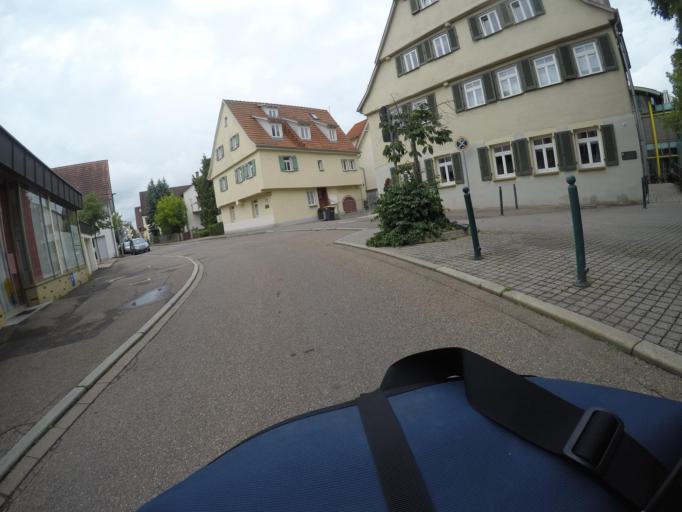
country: DE
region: Baden-Wuerttemberg
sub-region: Regierungsbezirk Stuttgart
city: Ditzingen
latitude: 48.8259
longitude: 9.0665
